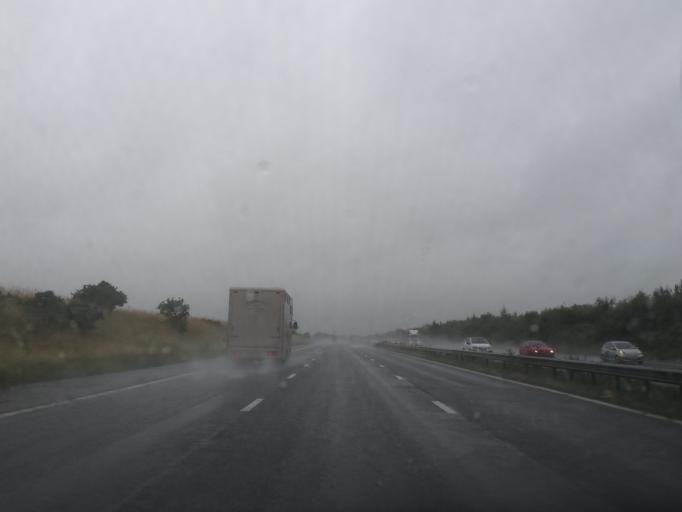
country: GB
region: England
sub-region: Leicestershire
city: Hinckley
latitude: 52.4855
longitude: -1.3932
